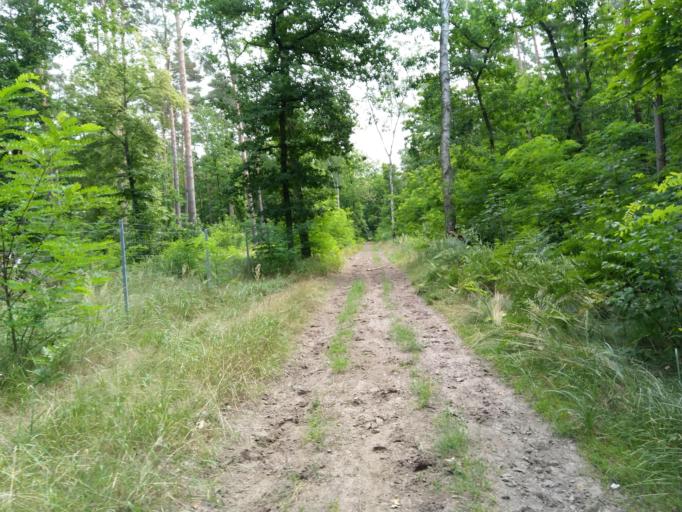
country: DE
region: Berlin
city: Friedrichshagen
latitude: 52.4646
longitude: 13.6526
